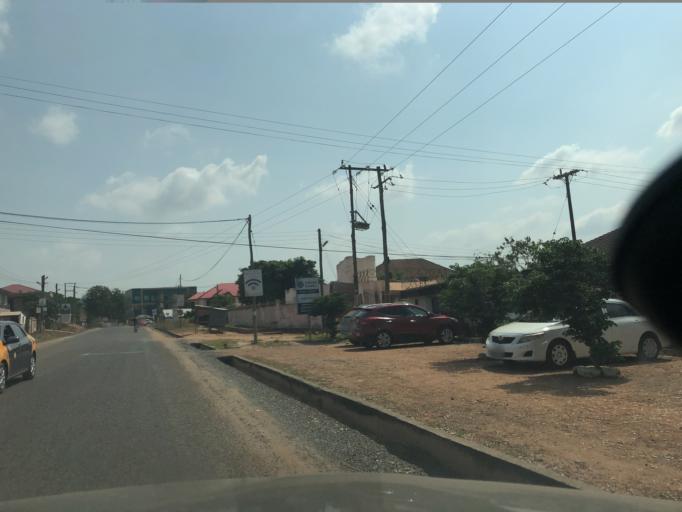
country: GH
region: Greater Accra
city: Medina Estates
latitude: 5.6809
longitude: -0.1943
